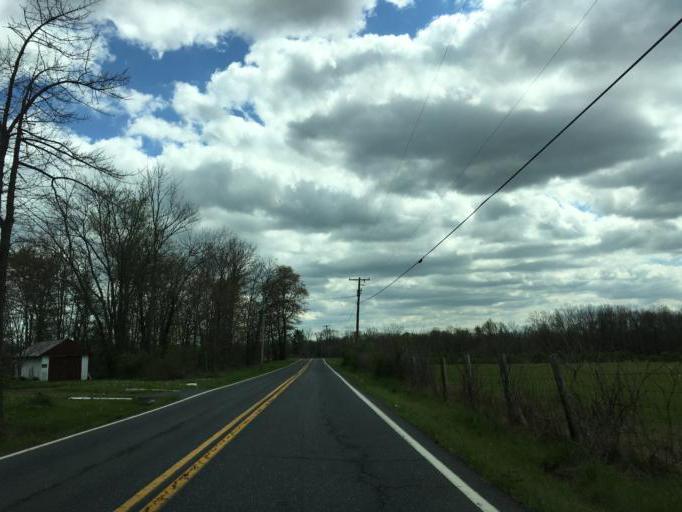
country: US
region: Maryland
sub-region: Frederick County
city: Thurmont
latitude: 39.5835
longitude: -77.3933
